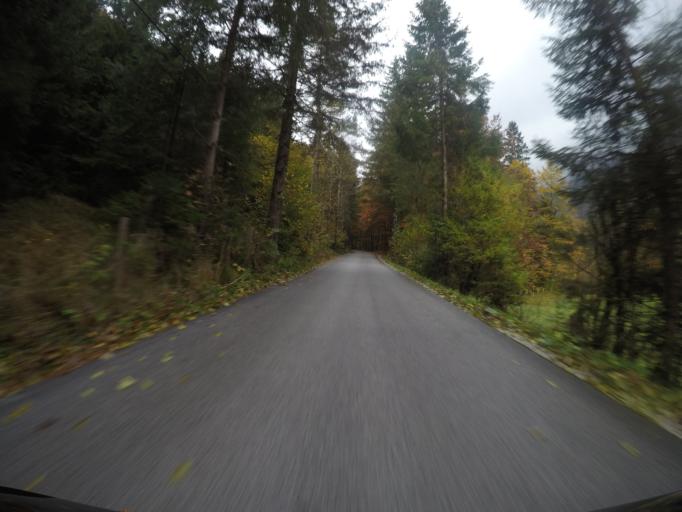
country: SI
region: Jesenice
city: Hrusica
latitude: 46.4072
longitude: 13.9986
